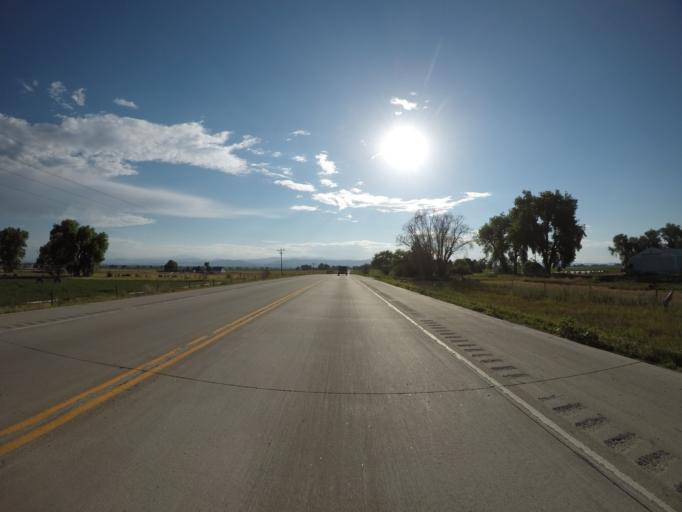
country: US
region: Colorado
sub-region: Weld County
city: Severance
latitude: 40.5811
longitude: -104.9387
